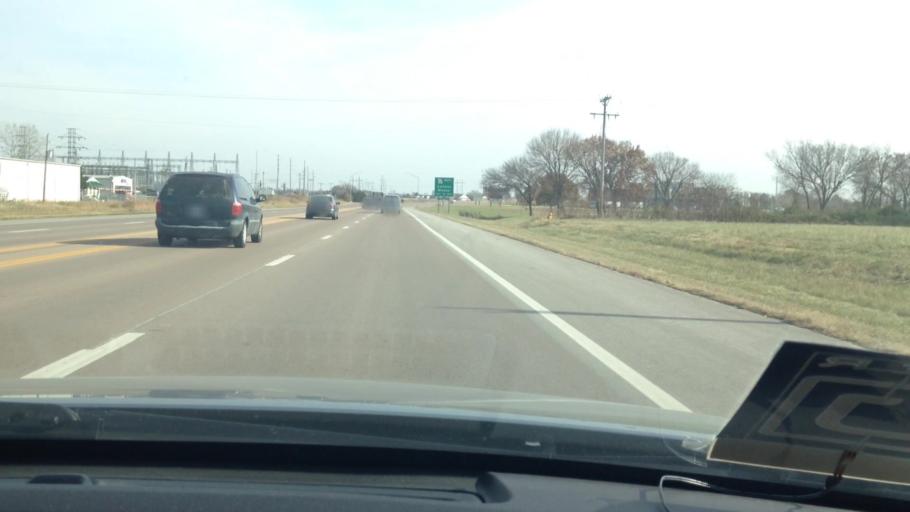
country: US
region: Missouri
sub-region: Henry County
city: Clinton
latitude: 38.3881
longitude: -93.7660
